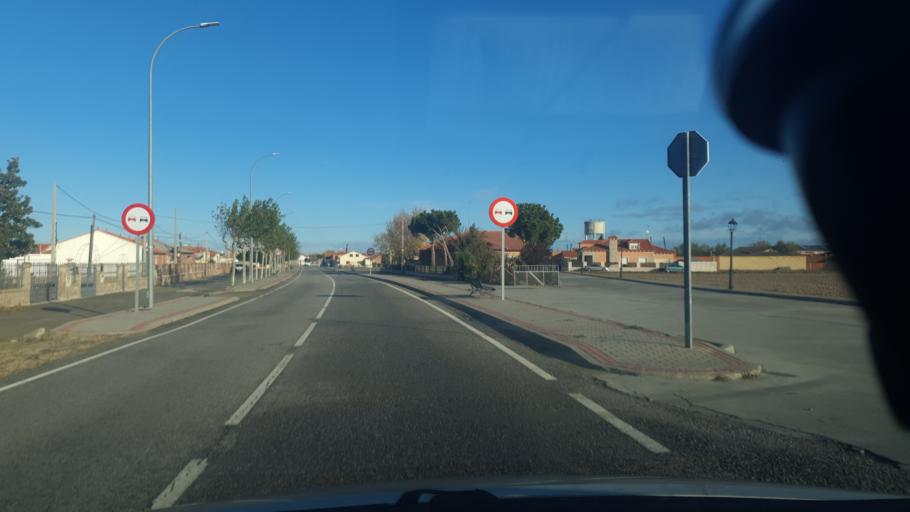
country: ES
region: Castille and Leon
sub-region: Provincia de Avila
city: Tinosillos
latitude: 40.9296
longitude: -4.7275
